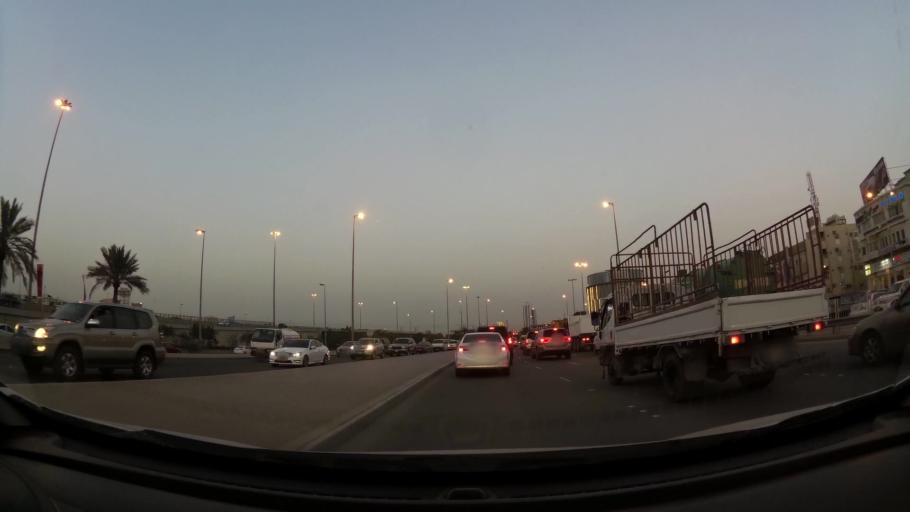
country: BH
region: Manama
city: Manama
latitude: 26.2035
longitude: 50.5646
